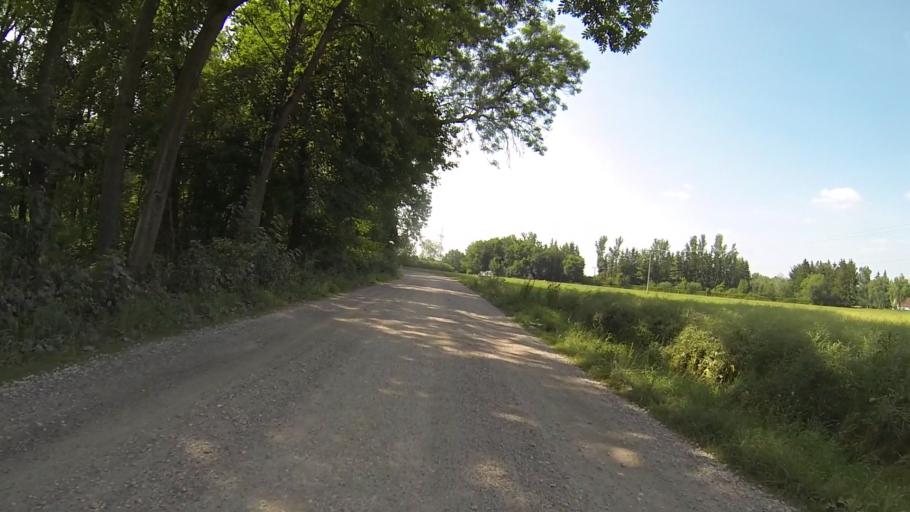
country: DE
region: Bavaria
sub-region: Swabia
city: Guenzburg
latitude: 48.4694
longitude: 10.2632
